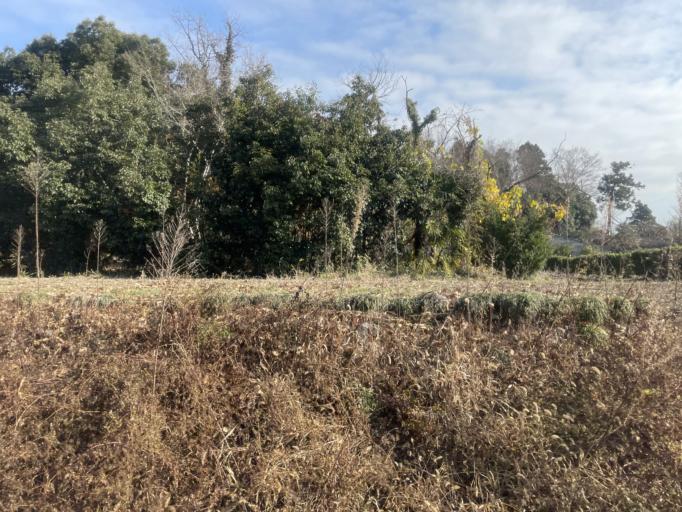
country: JP
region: Saitama
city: Yorii
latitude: 36.1124
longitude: 139.1844
